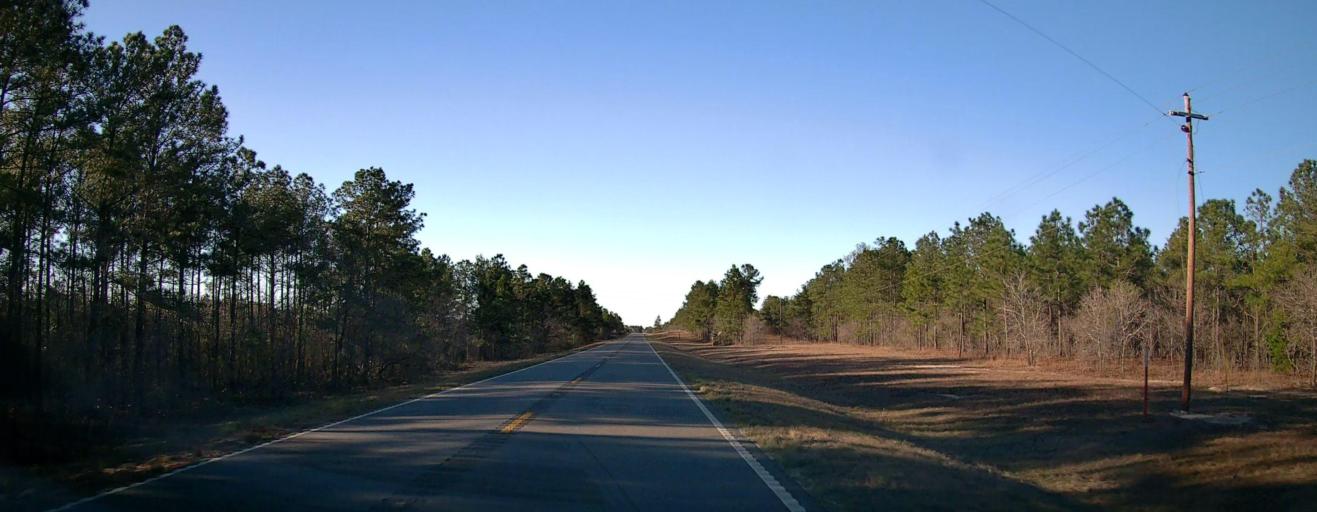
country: US
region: Georgia
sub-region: Talbot County
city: Talbotton
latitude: 32.5770
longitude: -84.4442
